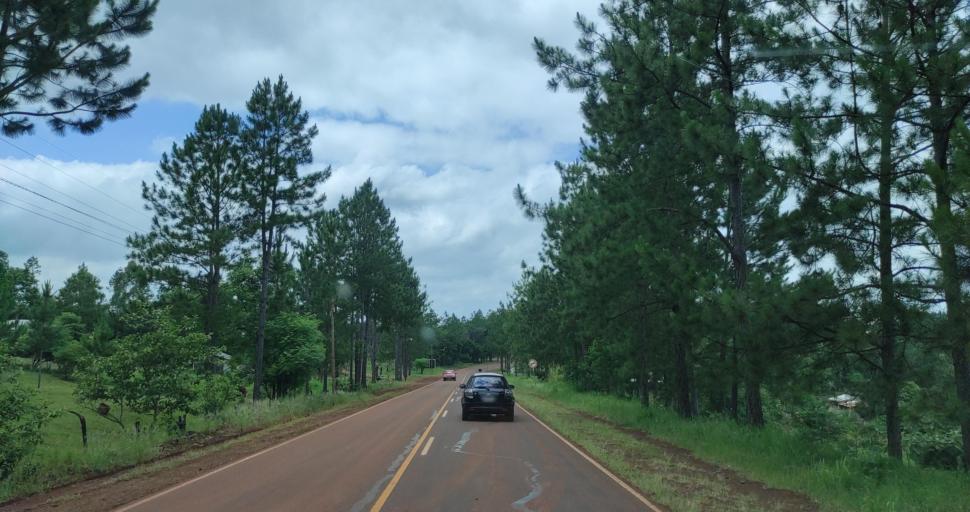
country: AR
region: Misiones
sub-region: Departamento de Veinticinco de Mayo
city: Veinticinco de Mayo
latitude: -27.4173
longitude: -54.7358
